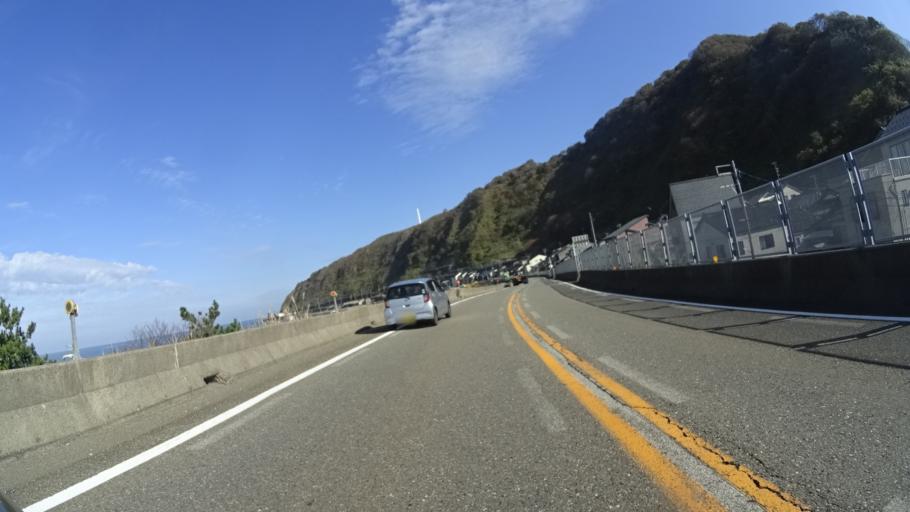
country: JP
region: Niigata
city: Joetsu
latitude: 37.1351
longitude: 138.0538
